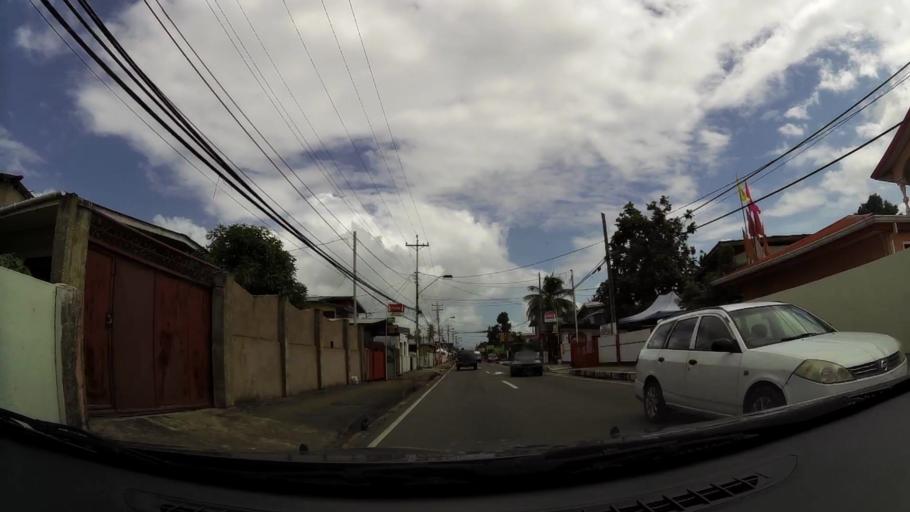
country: TT
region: Tunapuna/Piarco
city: Arouca
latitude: 10.6341
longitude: -61.3313
